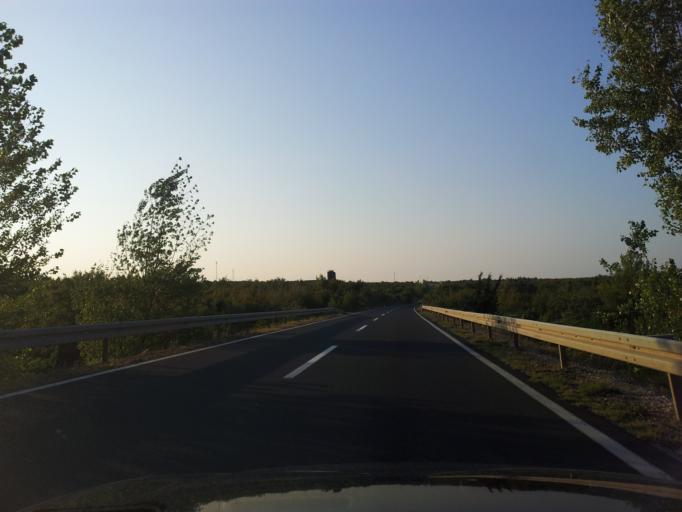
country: HR
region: Zadarska
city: Benkovac
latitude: 44.0115
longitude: 15.5731
